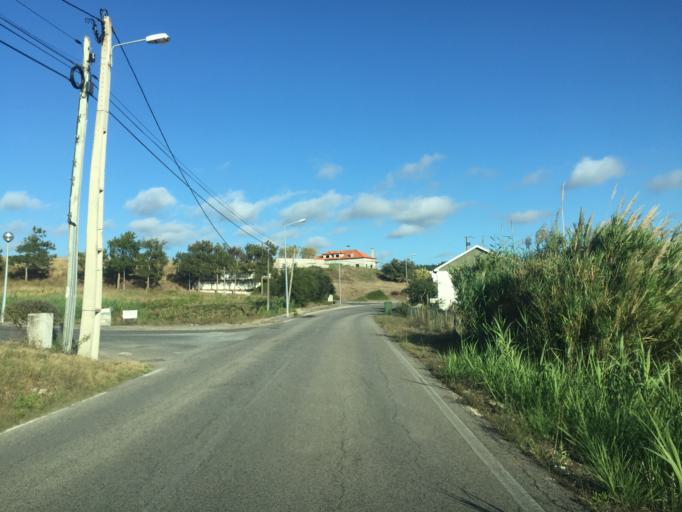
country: PT
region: Lisbon
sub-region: Torres Vedras
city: A dos Cunhados
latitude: 39.1573
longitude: -9.3012
